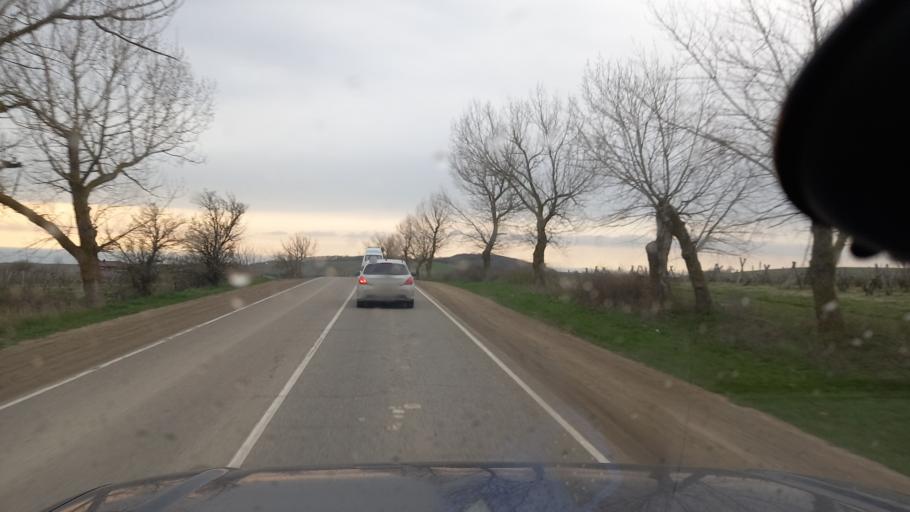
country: RU
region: Krasnodarskiy
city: Sukko
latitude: 44.8395
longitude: 37.3948
